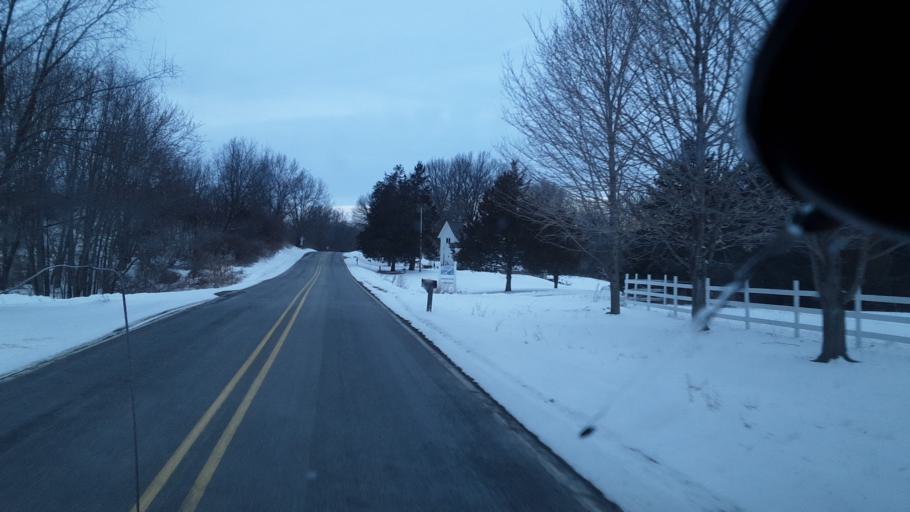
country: US
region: Michigan
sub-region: Ingham County
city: Leslie
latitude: 42.4432
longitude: -84.3225
